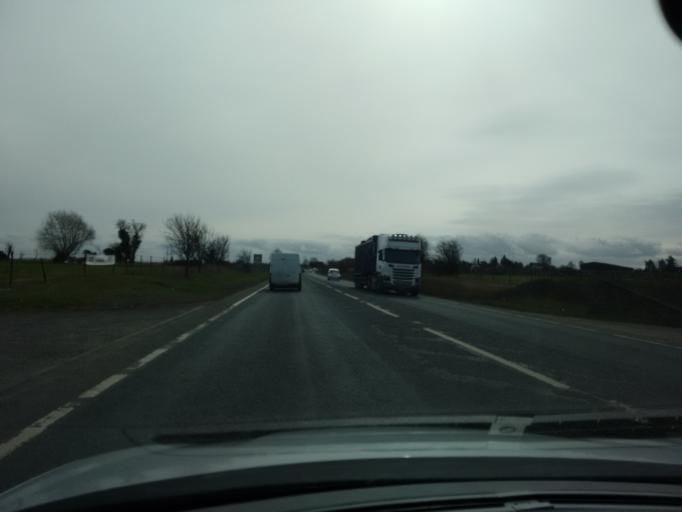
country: GB
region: England
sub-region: Worcestershire
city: Evesham
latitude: 52.1048
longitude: -1.9275
